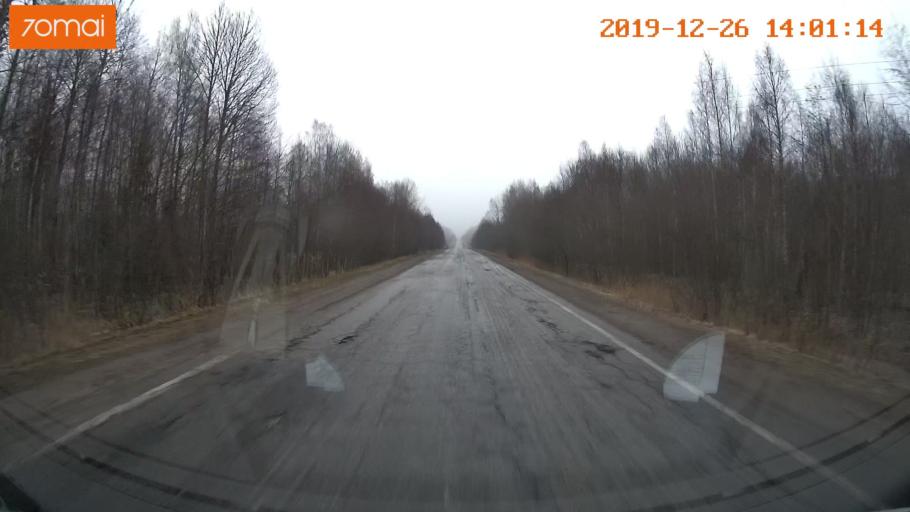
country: RU
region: Jaroslavl
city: Poshekhon'ye
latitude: 58.5520
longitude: 38.7599
